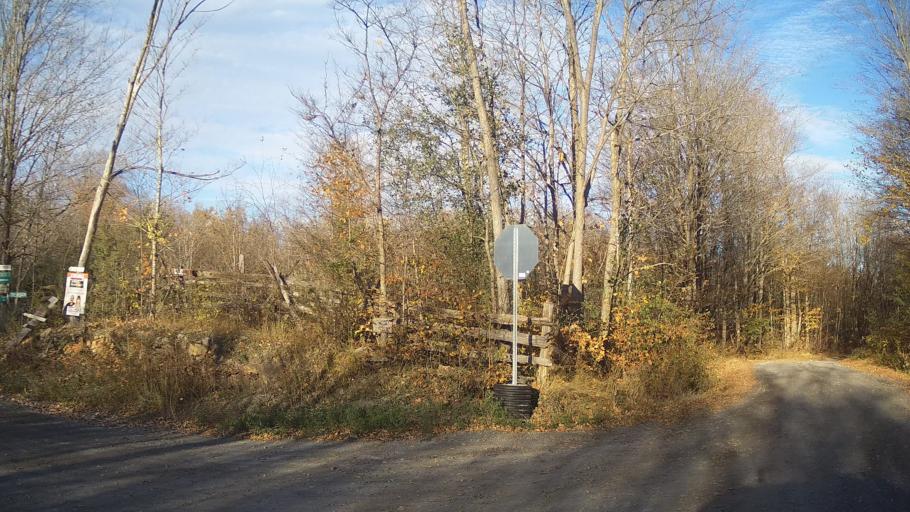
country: CA
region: Ontario
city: Perth
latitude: 44.7447
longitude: -76.4072
